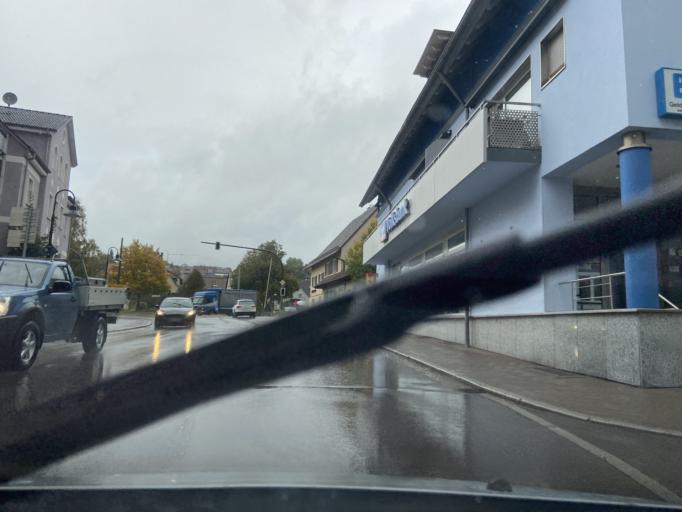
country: DE
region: Baden-Wuerttemberg
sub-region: Tuebingen Region
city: Sigmaringendorf
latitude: 48.0674
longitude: 9.2619
